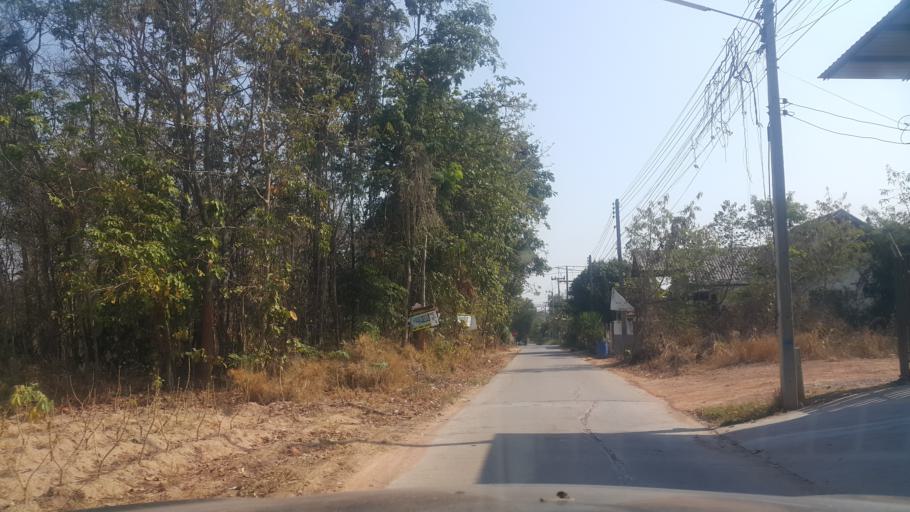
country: TH
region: Nakhon Ratchasima
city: Nakhon Ratchasima
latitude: 14.9327
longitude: 102.0426
